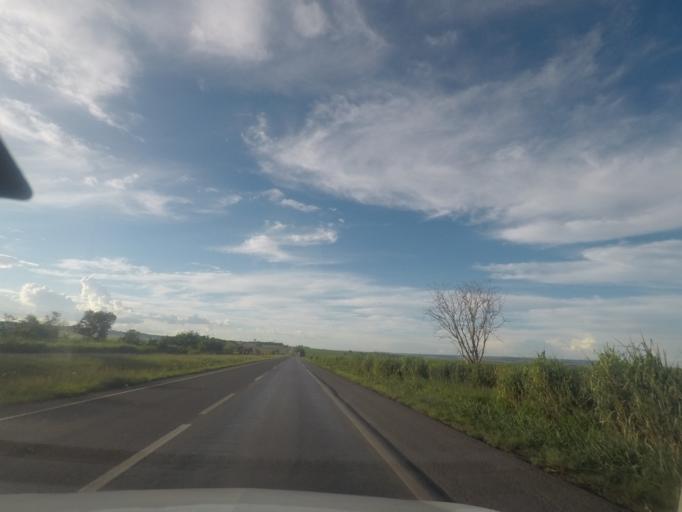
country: BR
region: Goias
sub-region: Goiatuba
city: Goiatuba
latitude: -18.2101
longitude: -49.2744
